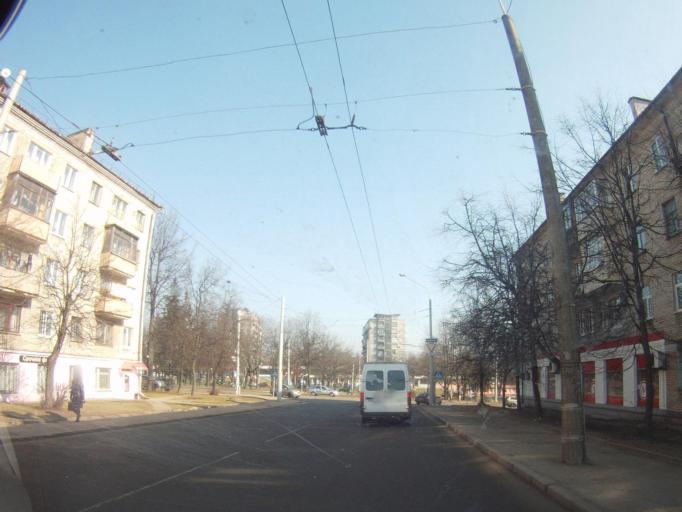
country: BY
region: Minsk
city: Minsk
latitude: 53.9288
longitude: 27.6096
